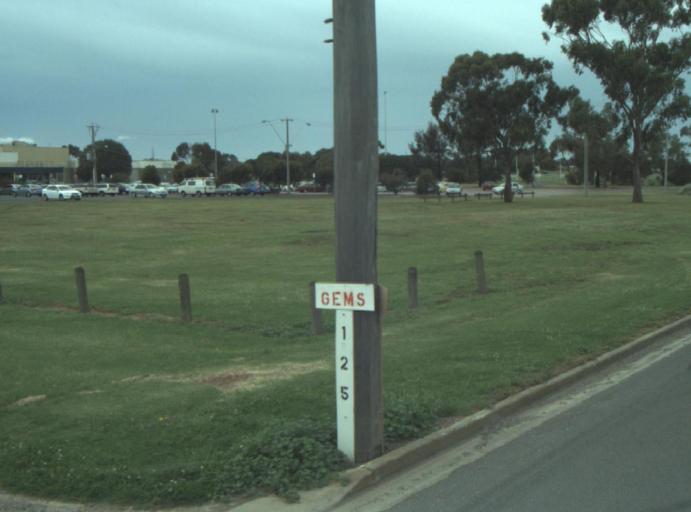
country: AU
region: Victoria
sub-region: Greater Geelong
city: Breakwater
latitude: -38.1773
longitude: 144.4018
